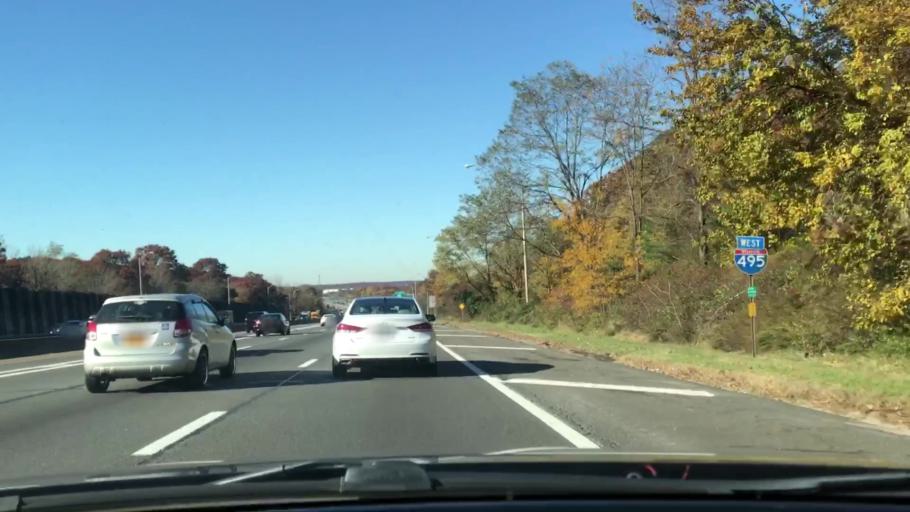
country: US
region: New York
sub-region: Suffolk County
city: Wheatley Heights
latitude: 40.7880
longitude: -73.3801
